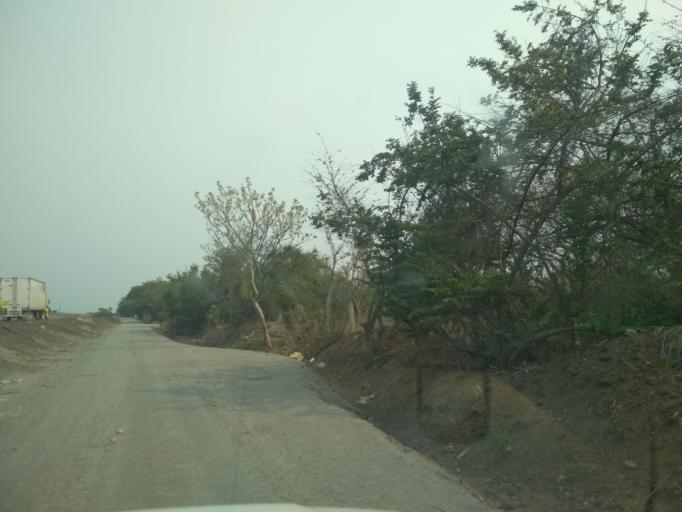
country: MX
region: Veracruz
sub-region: Veracruz
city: Hacienda Sotavento
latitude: 19.1032
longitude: -96.2181
